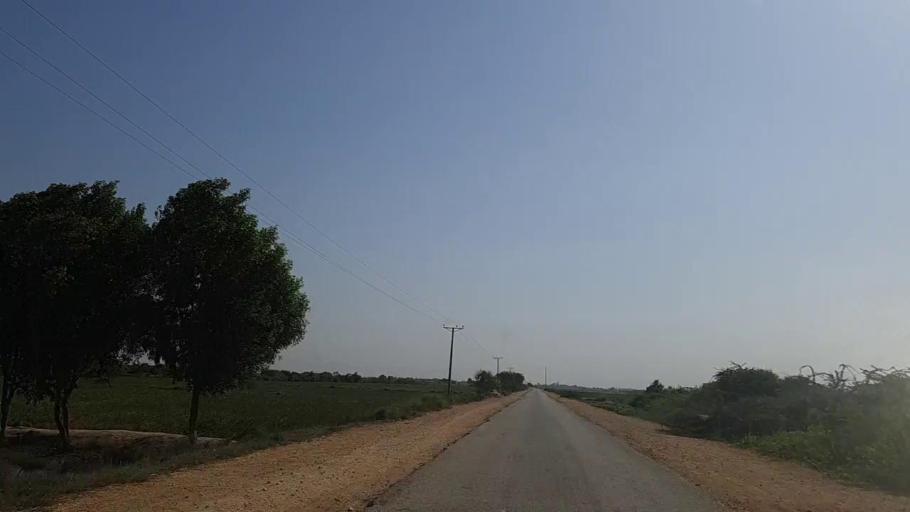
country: PK
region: Sindh
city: Mirpur Batoro
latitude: 24.6339
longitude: 68.2924
